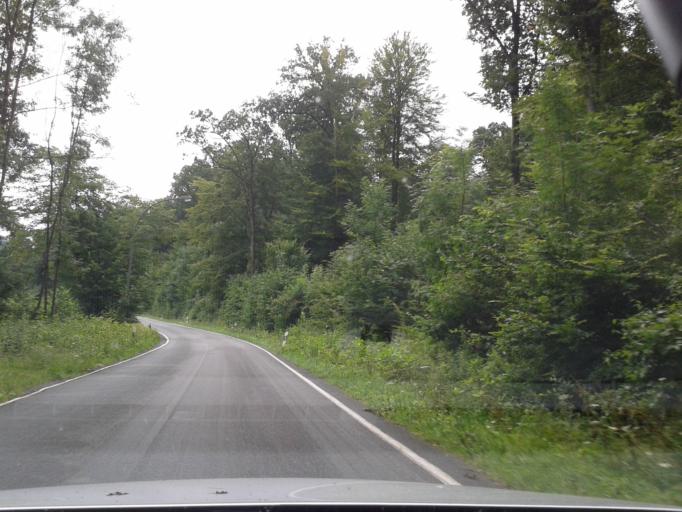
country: DE
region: North Rhine-Westphalia
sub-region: Regierungsbezirk Detmold
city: Blomberg
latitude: 51.9341
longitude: 9.1498
